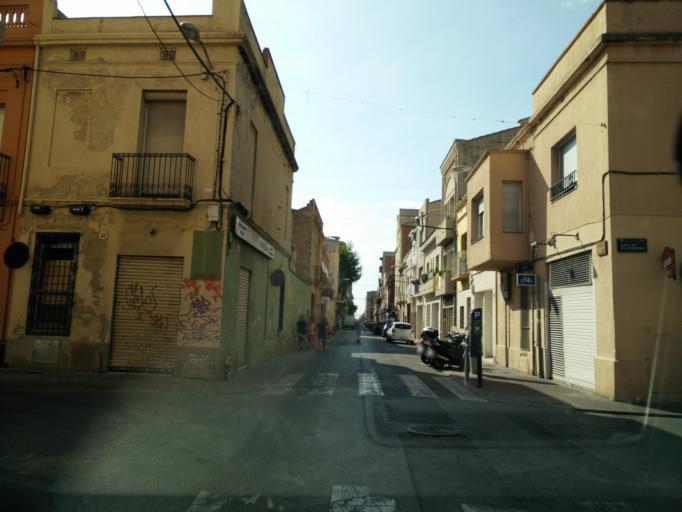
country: ES
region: Catalonia
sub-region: Provincia de Barcelona
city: Badalona
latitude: 41.4451
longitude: 2.2418
